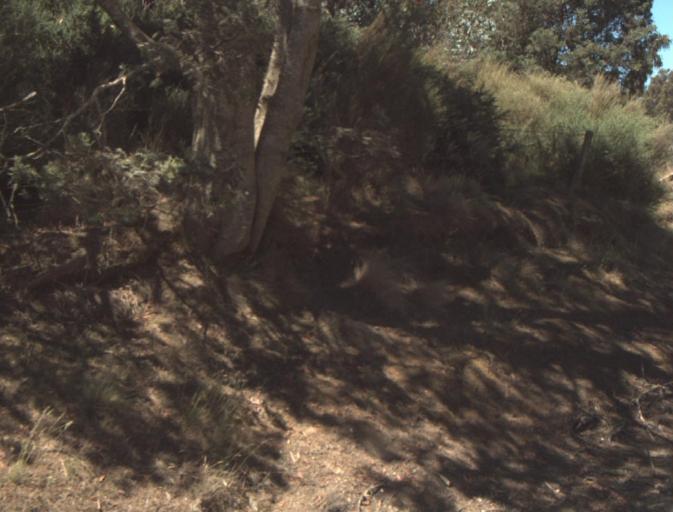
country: AU
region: Tasmania
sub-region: Dorset
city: Scottsdale
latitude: -41.3241
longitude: 147.4666
